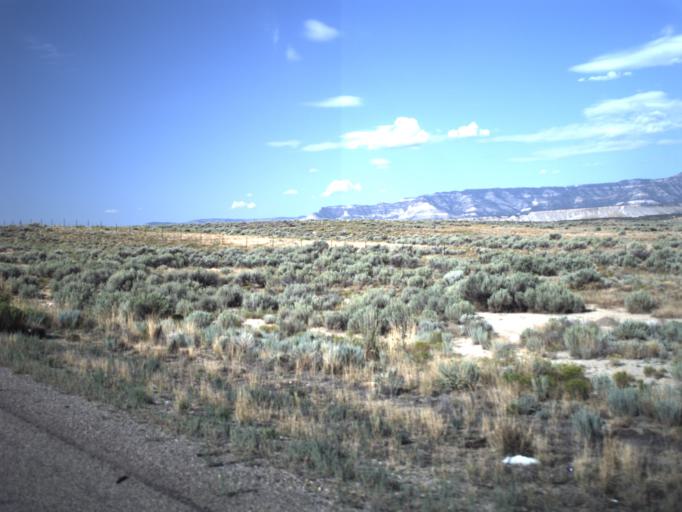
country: US
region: Utah
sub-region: Carbon County
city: Price
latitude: 39.4860
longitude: -110.8501
